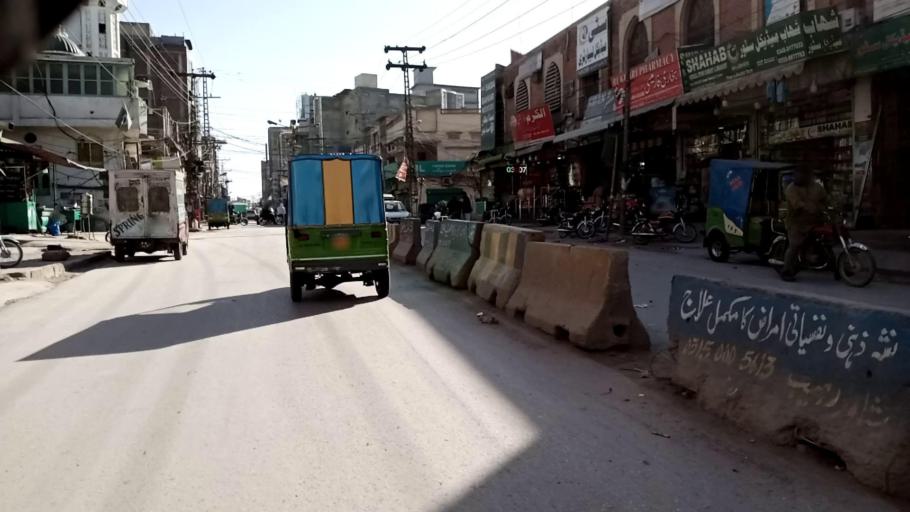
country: PK
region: Khyber Pakhtunkhwa
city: Peshawar
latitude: 34.0041
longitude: 71.5602
